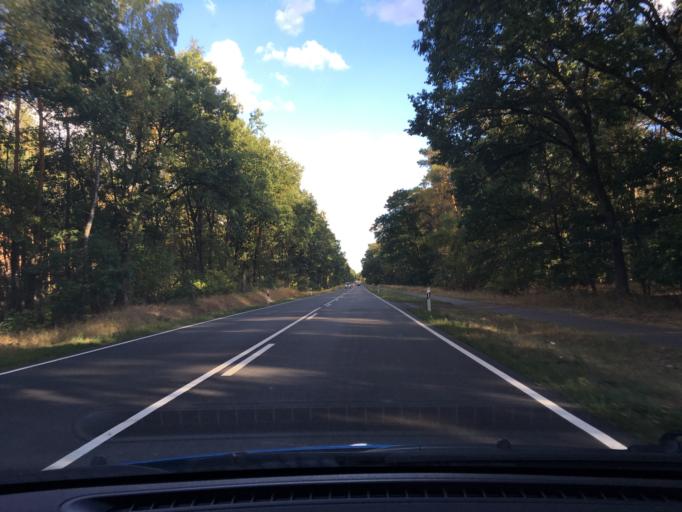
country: DE
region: Mecklenburg-Vorpommern
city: Grabow
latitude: 53.2924
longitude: 11.5432
